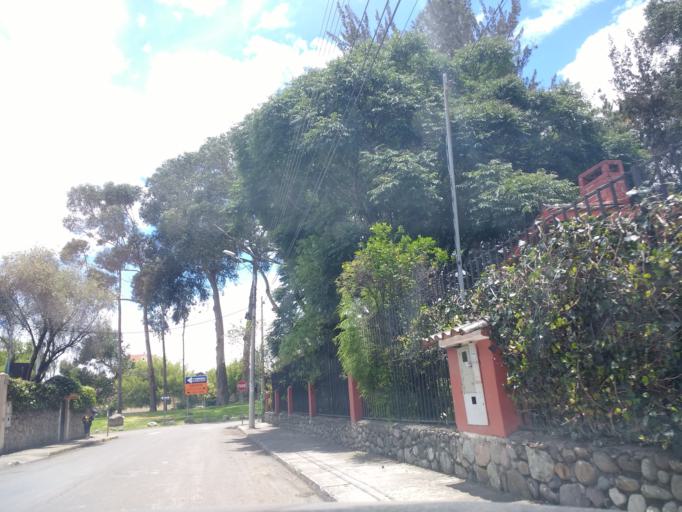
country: EC
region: Azuay
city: Cuenca
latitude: -2.8932
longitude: -79.0262
